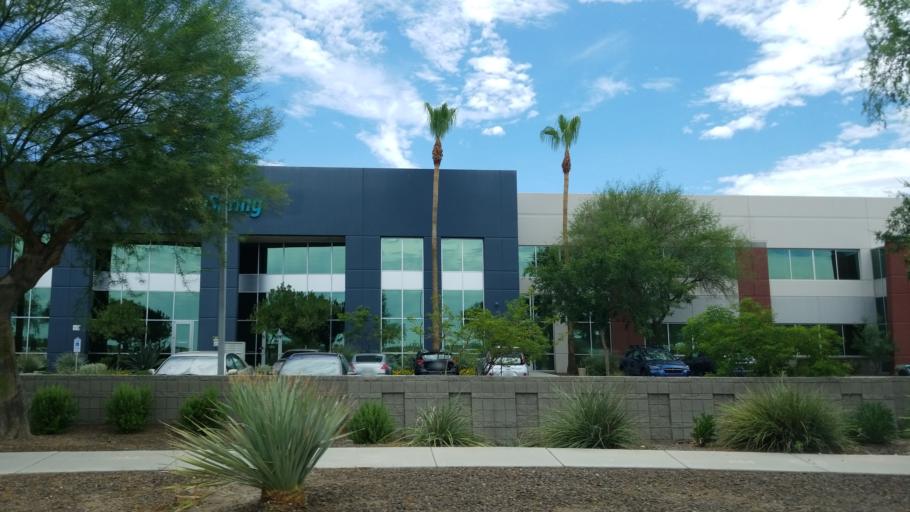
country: US
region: Arizona
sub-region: Maricopa County
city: Anthem
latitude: 33.7022
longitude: -112.1087
